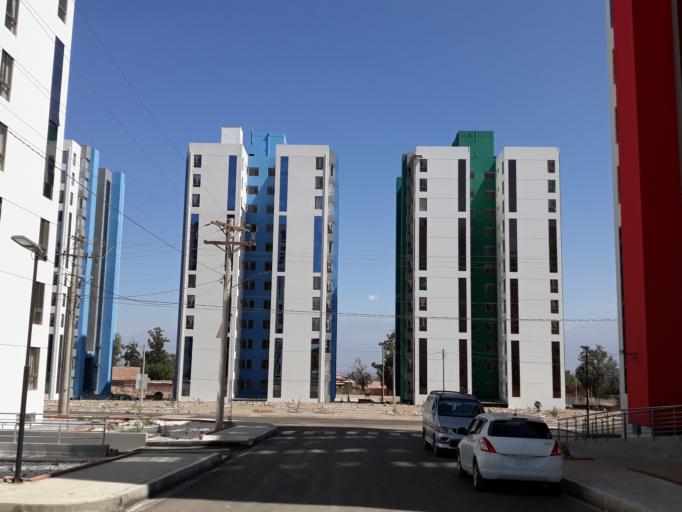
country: BO
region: Cochabamba
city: Cochabamba
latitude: -17.4643
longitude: -66.1396
